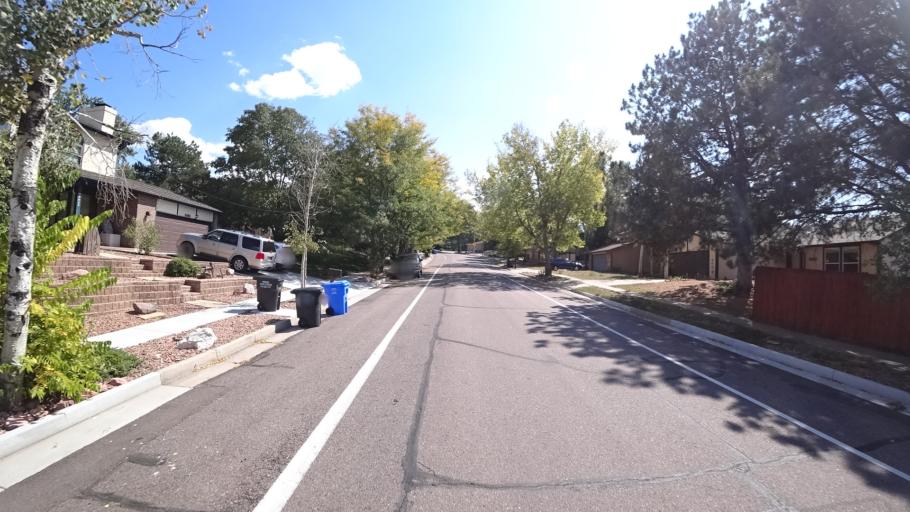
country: US
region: Colorado
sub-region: El Paso County
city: Cimarron Hills
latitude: 38.8736
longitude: -104.7452
